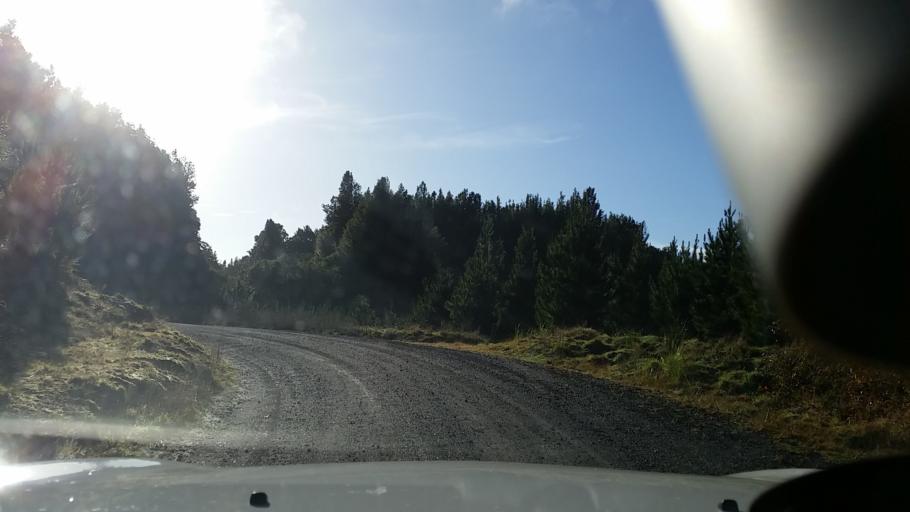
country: NZ
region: Bay of Plenty
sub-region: Kawerau District
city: Kawerau
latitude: -38.0307
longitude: 176.5555
